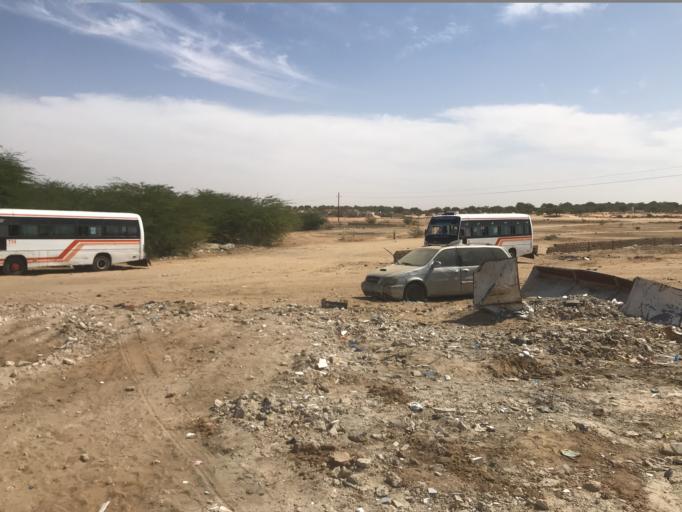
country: SN
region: Saint-Louis
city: Saint-Louis
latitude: 16.0601
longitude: -16.4164
